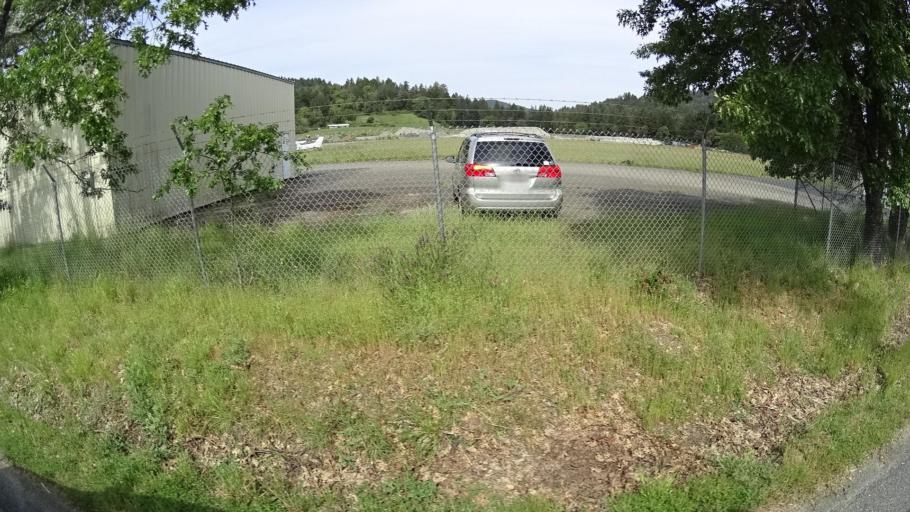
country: US
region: California
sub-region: Humboldt County
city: Redway
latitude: 40.0869
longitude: -123.8119
